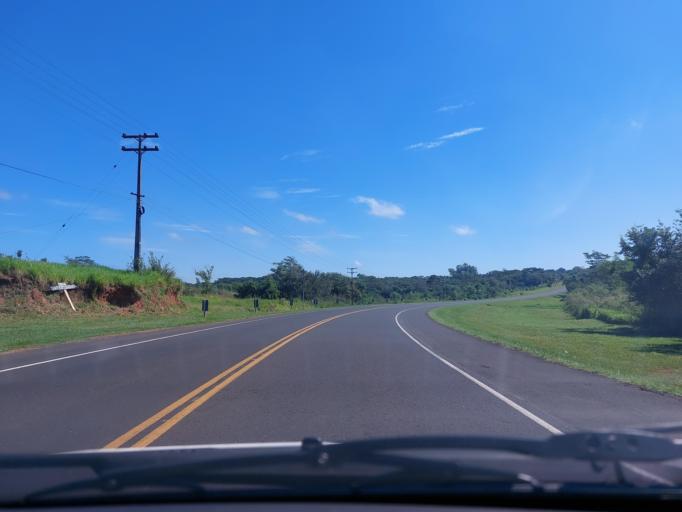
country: PY
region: San Pedro
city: Guayaybi
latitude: -24.6019
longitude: -56.5008
